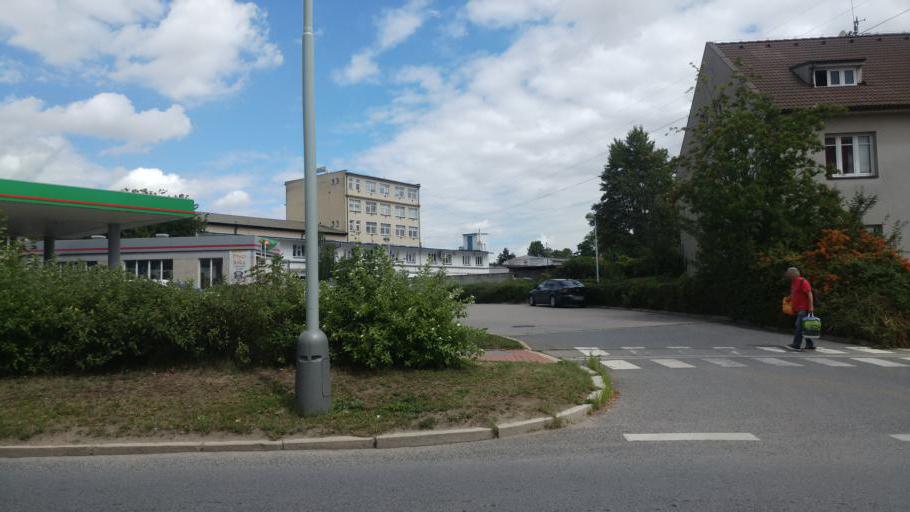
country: CZ
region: Praha
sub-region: Praha 8
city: Liben
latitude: 50.0642
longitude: 14.4940
